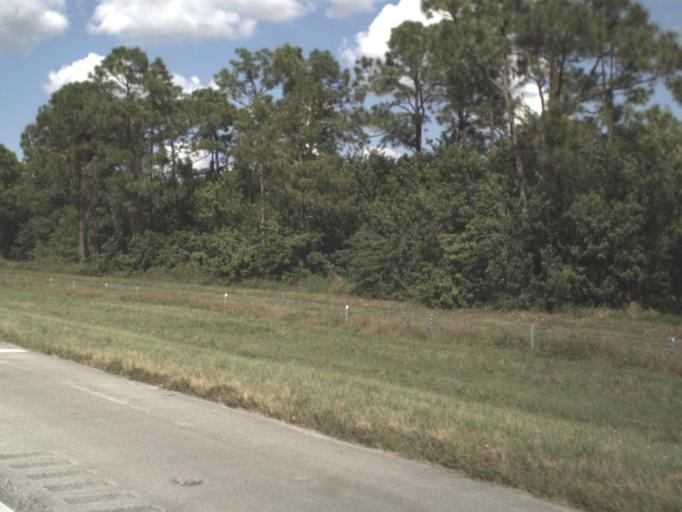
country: US
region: Florida
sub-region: Indian River County
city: West Vero Corridor
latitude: 27.5221
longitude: -80.5984
